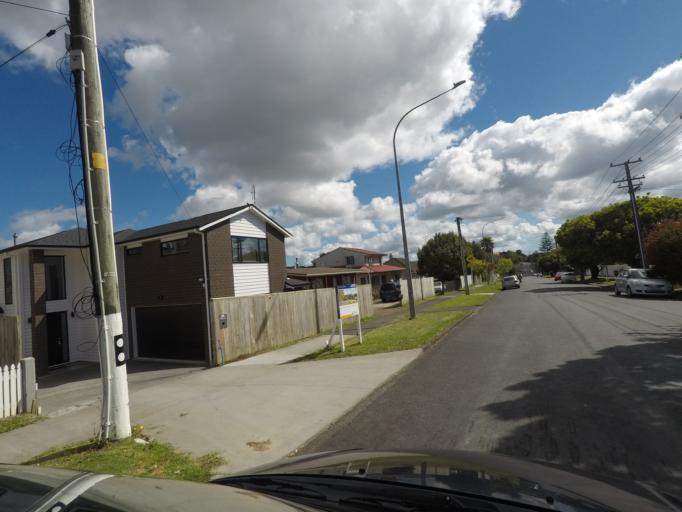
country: NZ
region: Auckland
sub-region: Auckland
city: Waitakere
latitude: -36.9144
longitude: 174.6655
